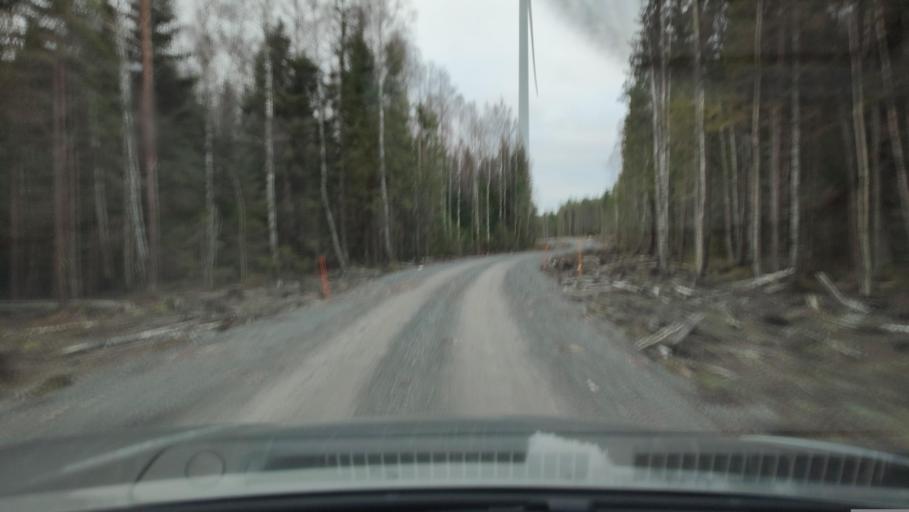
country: FI
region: Southern Ostrobothnia
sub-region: Suupohja
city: Karijoki
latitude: 62.1830
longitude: 21.5735
